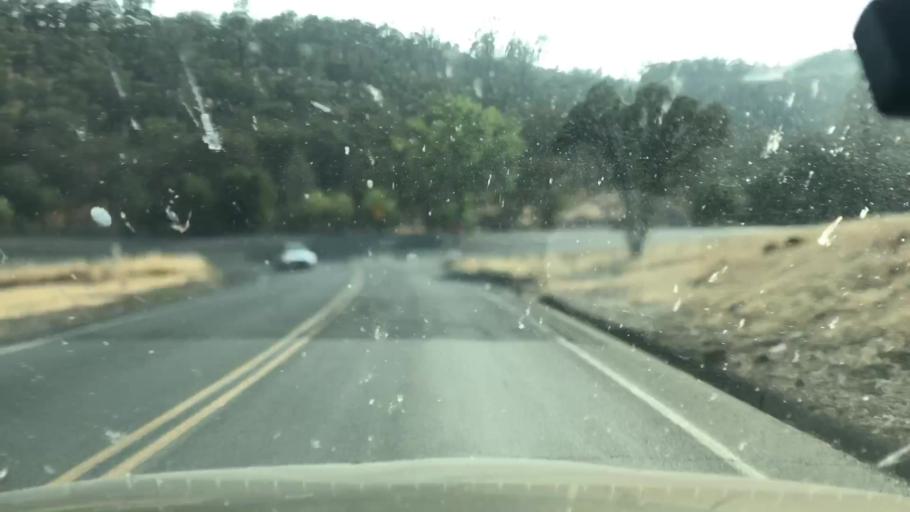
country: US
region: California
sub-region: Lake County
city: Hidden Valley Lake
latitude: 38.8203
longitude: -122.5759
